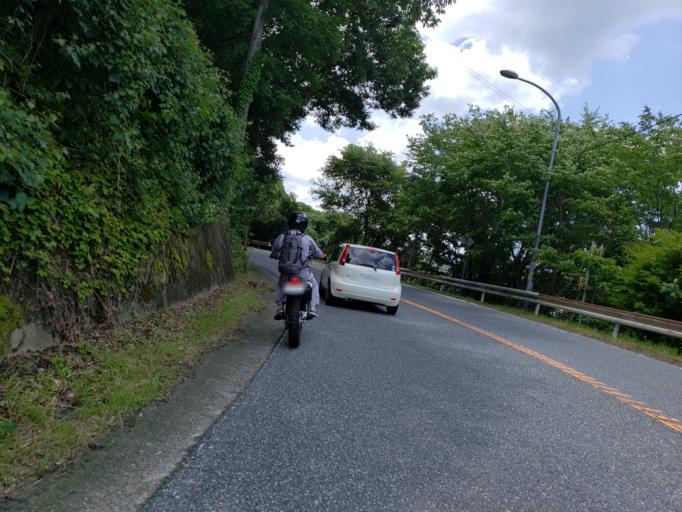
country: JP
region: Hyogo
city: Aioi
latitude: 34.8015
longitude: 134.4529
